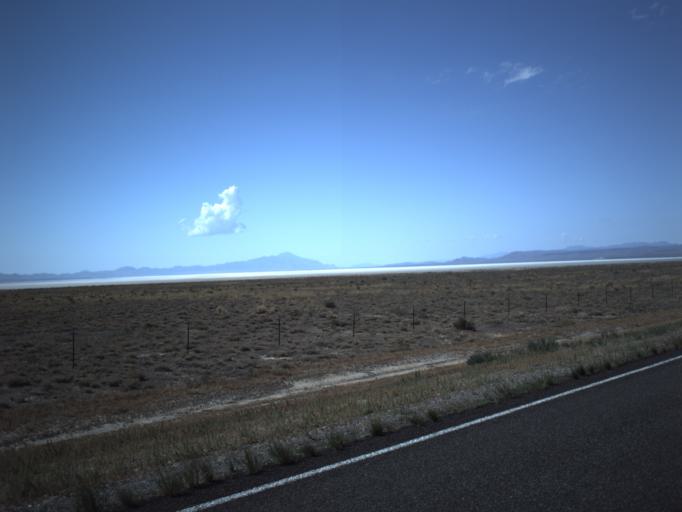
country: US
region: Utah
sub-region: Millard County
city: Delta
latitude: 39.1232
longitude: -113.1155
